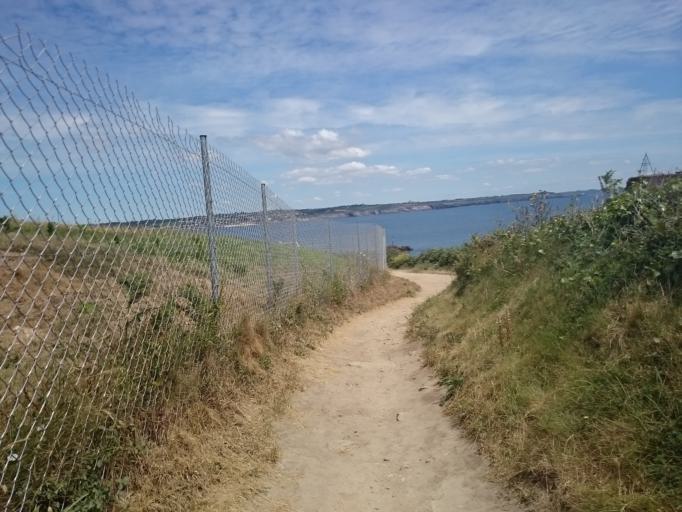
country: FR
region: Brittany
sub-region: Departement du Finistere
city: Plougonvelin
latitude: 48.3371
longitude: -4.7001
